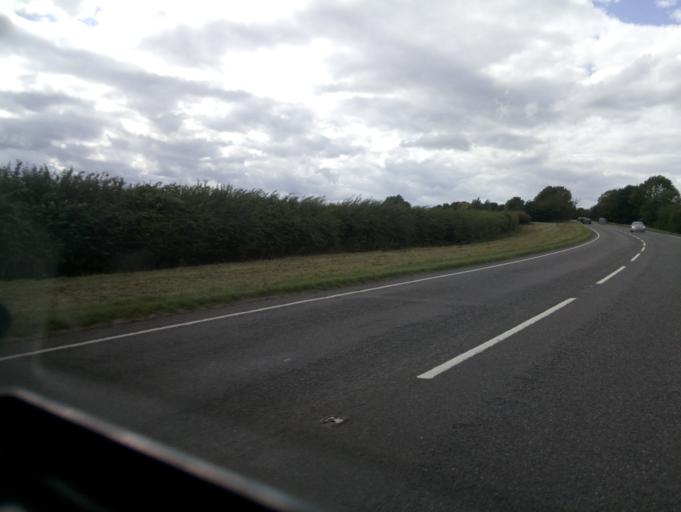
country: GB
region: England
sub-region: Leicestershire
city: Measham
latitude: 52.6372
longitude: -1.4950
